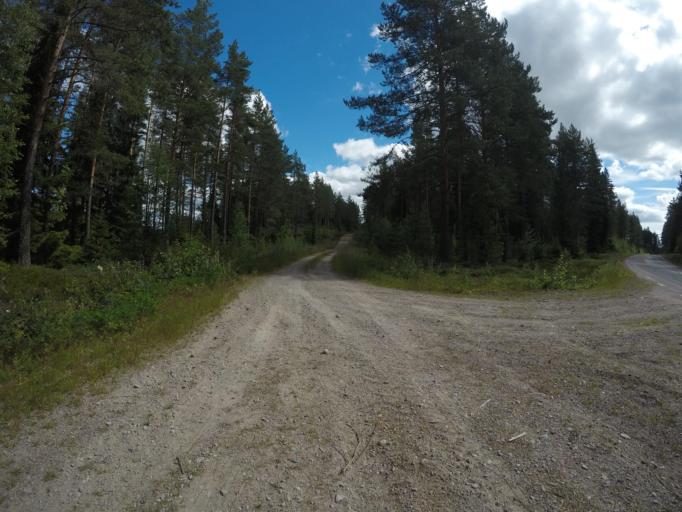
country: SE
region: OErebro
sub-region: Hallefors Kommun
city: Haellefors
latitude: 60.0698
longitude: 14.4931
